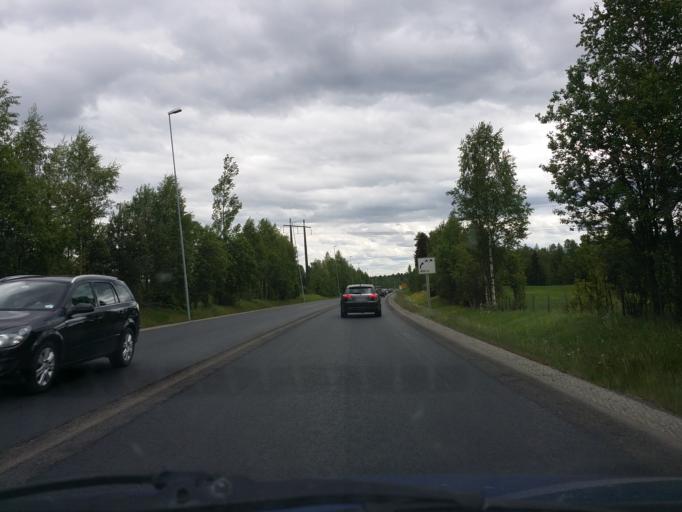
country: NO
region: Hedmark
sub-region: Hamar
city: Hamar
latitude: 60.8393
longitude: 11.0673
